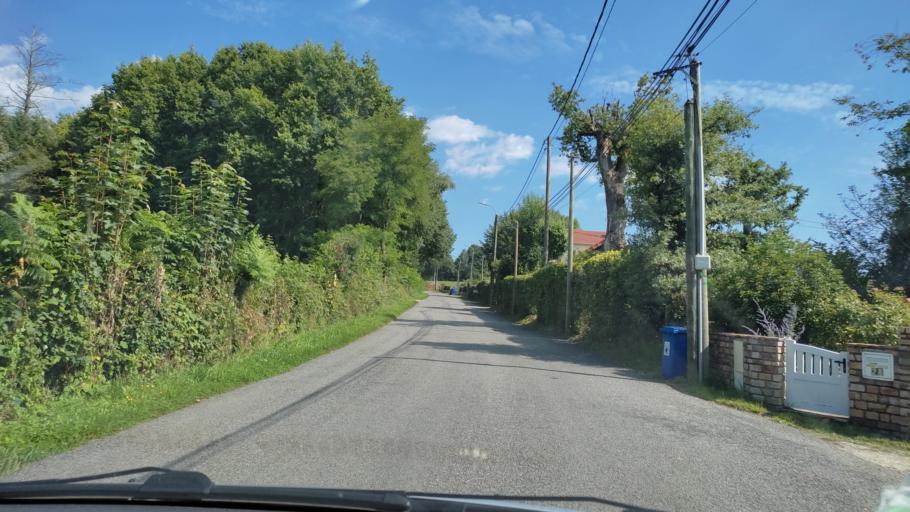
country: FR
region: Limousin
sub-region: Departement de la Haute-Vienne
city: Isle
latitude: 45.8471
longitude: 1.1923
